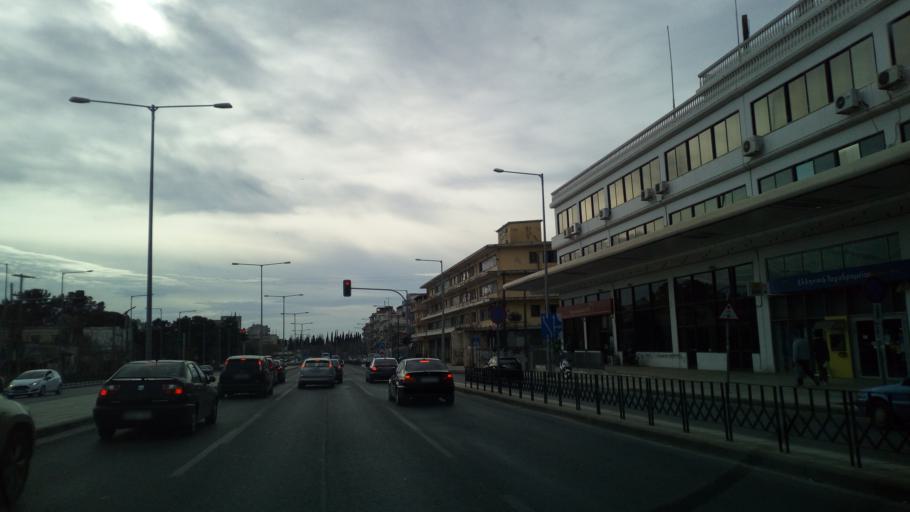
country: GR
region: Central Macedonia
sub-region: Nomos Thessalonikis
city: Stavroupoli
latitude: 40.6602
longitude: 22.9352
